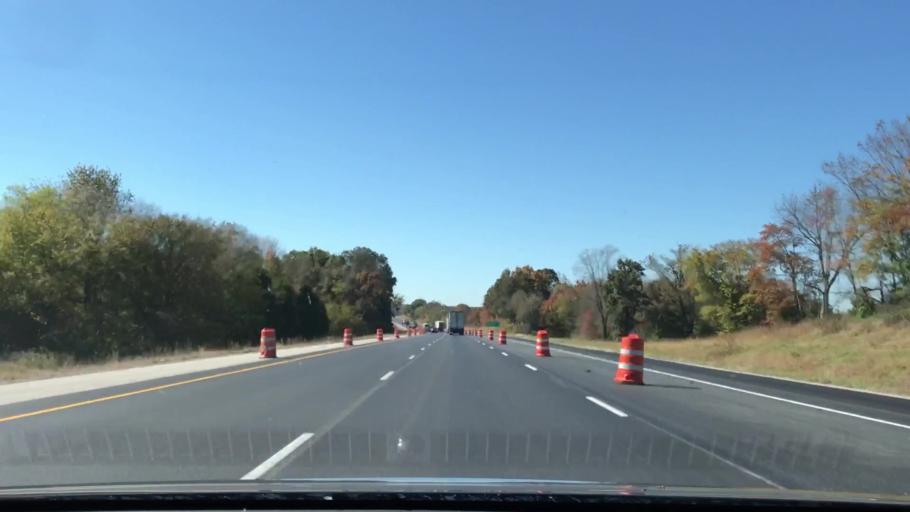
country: US
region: Kentucky
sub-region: Edmonson County
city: Brownsville
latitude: 37.0542
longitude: -86.1342
